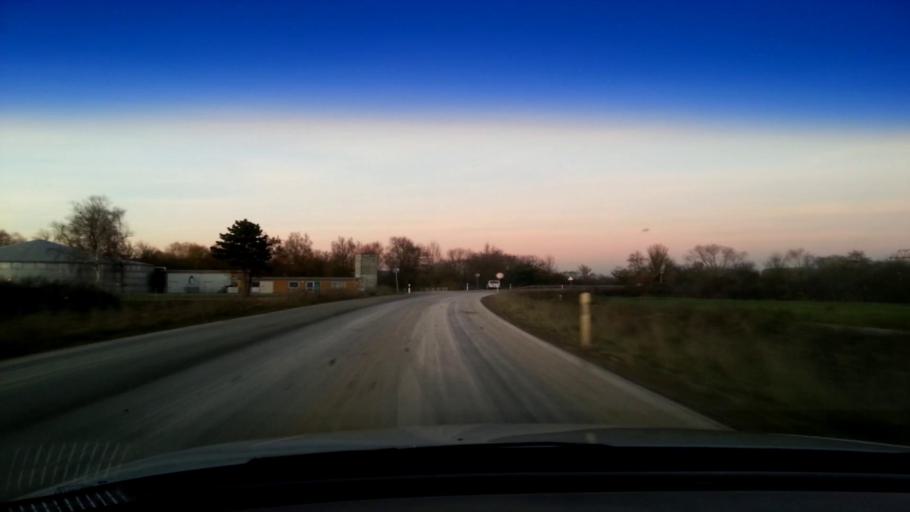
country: DE
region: Bavaria
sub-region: Upper Franconia
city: Zapfendorf
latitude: 50.0185
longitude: 10.9240
